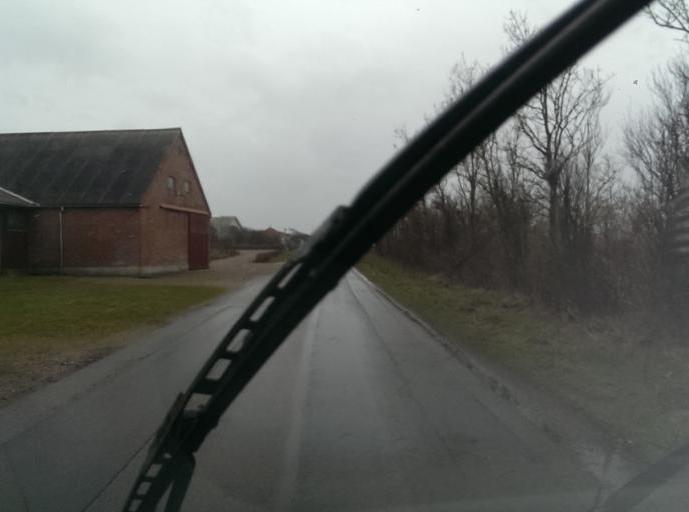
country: DK
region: Central Jutland
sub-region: Ringkobing-Skjern Kommune
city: Skjern
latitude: 56.0093
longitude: 8.4175
